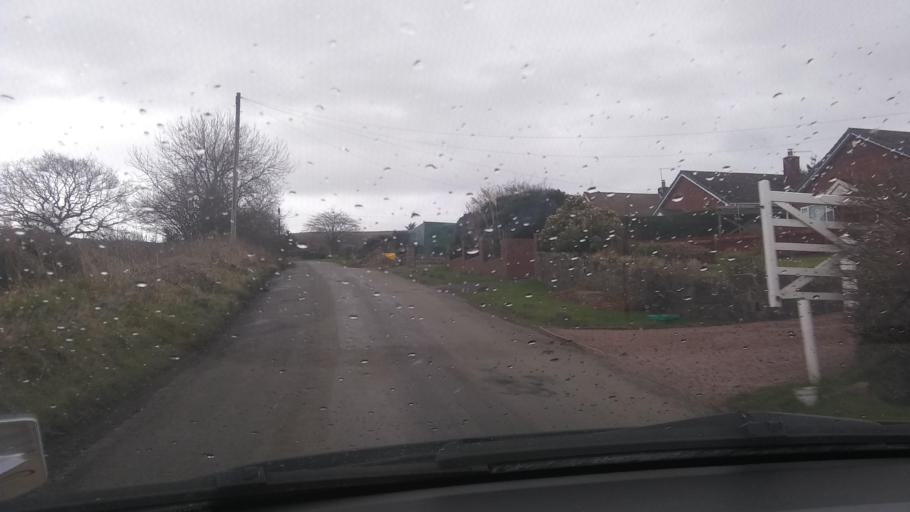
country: GB
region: England
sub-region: Worcestershire
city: Tenbury Wells
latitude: 52.3791
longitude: -2.6183
